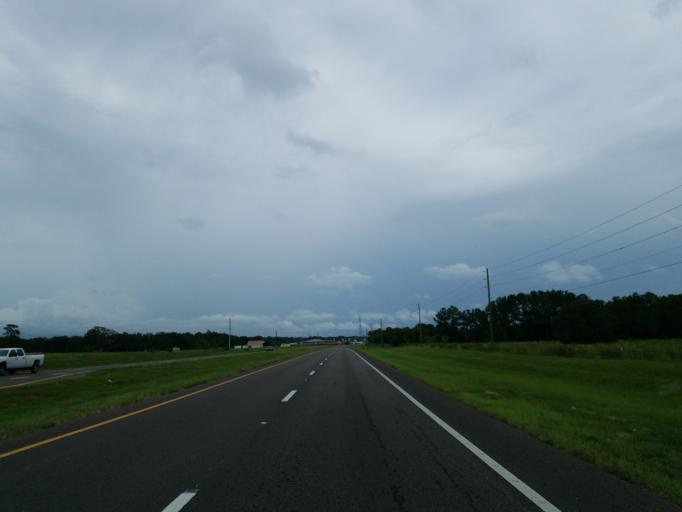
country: US
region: Florida
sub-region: Sumter County
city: Wildwood
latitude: 28.8769
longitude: -82.1056
